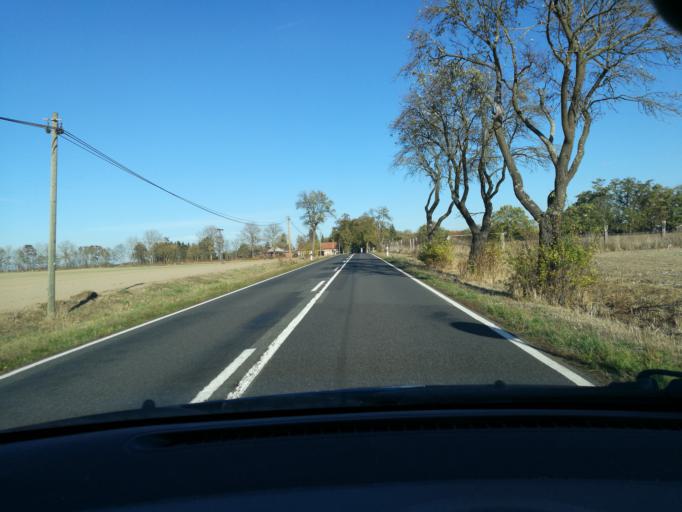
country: DE
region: Brandenburg
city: Lanz
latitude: 53.1477
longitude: 11.5753
